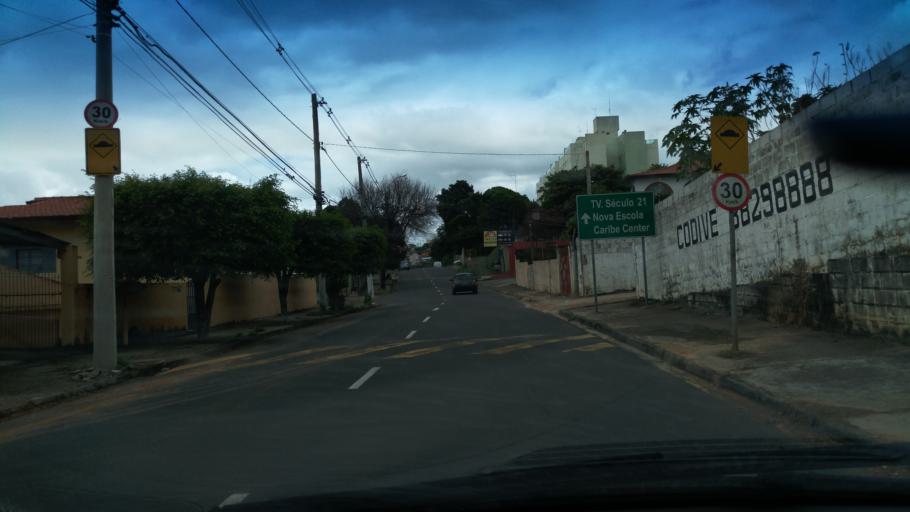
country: BR
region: Sao Paulo
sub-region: Valinhos
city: Valinhos
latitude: -22.9611
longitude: -47.0031
